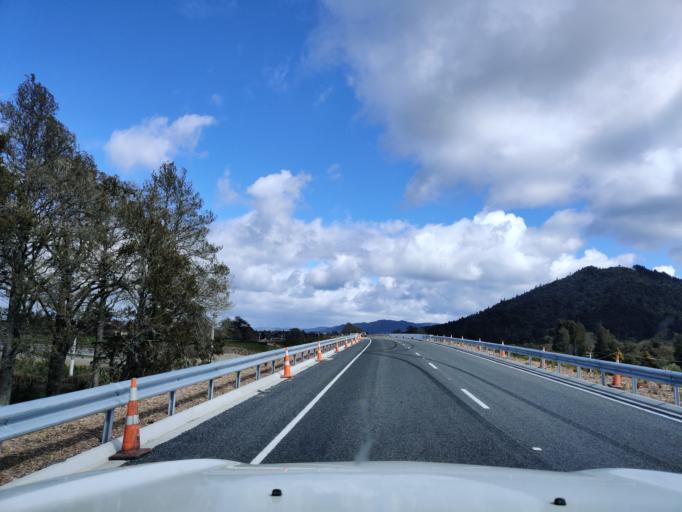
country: NZ
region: Waikato
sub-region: Waikato District
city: Ngaruawahia
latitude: -37.5957
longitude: 175.2059
